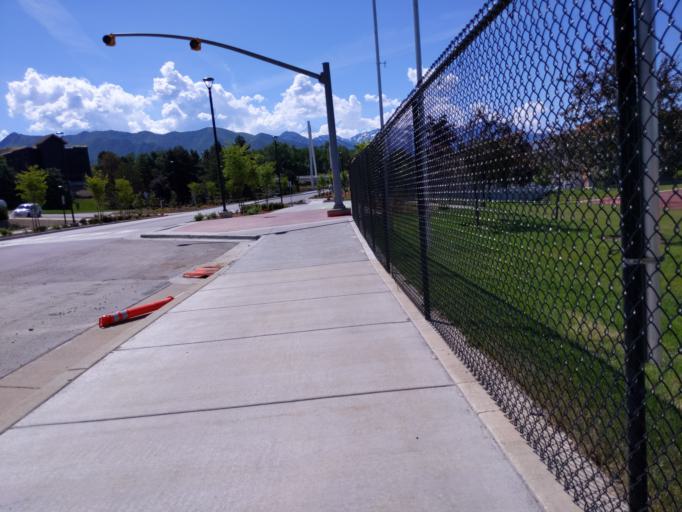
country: US
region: Utah
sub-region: Salt Lake County
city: Salt Lake City
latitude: 40.7670
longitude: -111.8385
